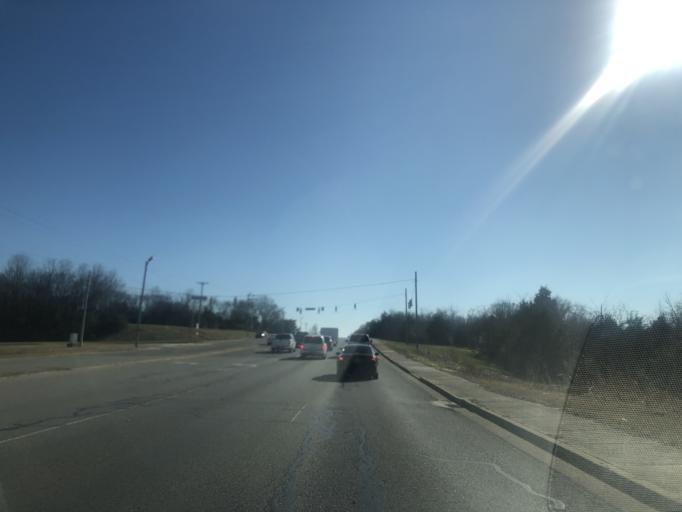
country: US
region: Tennessee
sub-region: Rutherford County
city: Smyrna
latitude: 35.9537
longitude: -86.5143
